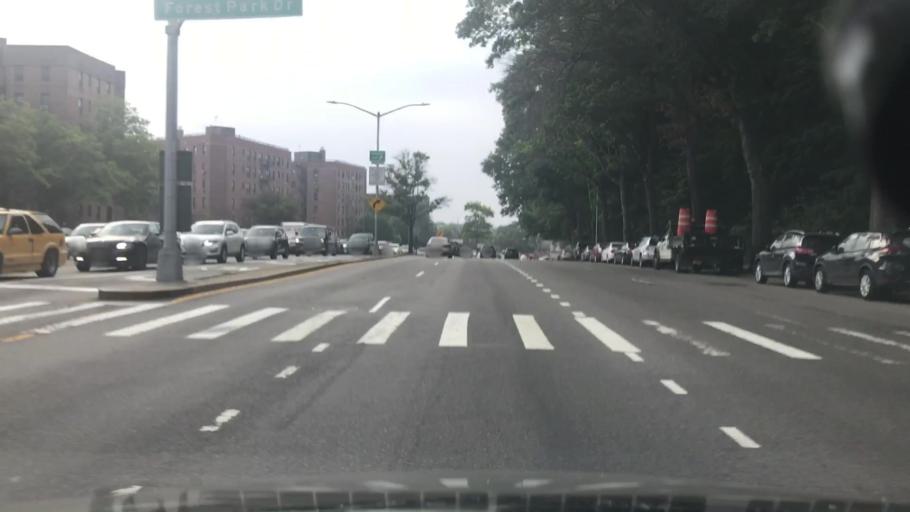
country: US
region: New York
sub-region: Queens County
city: Borough of Queens
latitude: 40.7006
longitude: -73.8547
